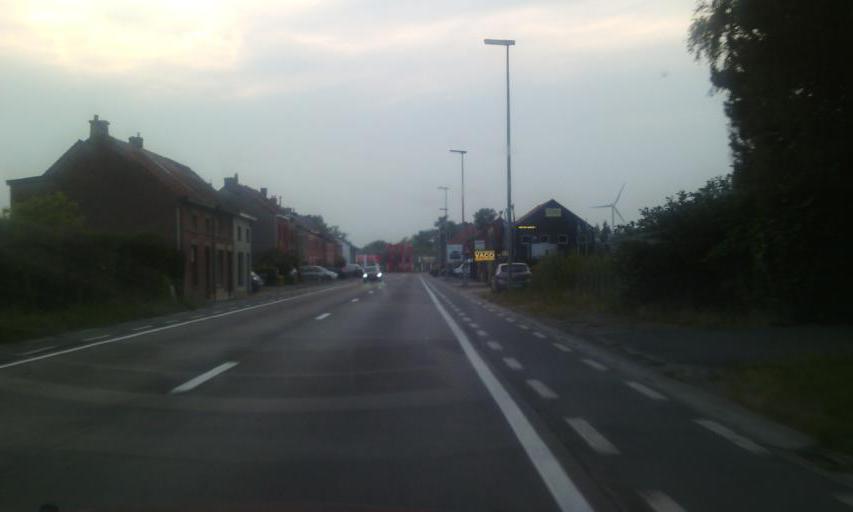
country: BE
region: Flanders
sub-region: Provincie Oost-Vlaanderen
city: Dendermonde
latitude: 51.0445
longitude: 4.0943
